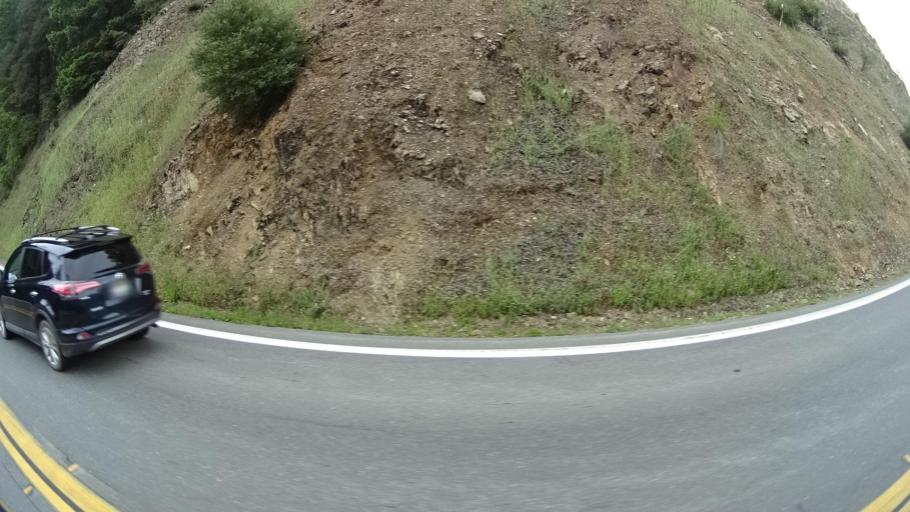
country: US
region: California
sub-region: Humboldt County
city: Willow Creek
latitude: 40.9947
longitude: -123.6315
